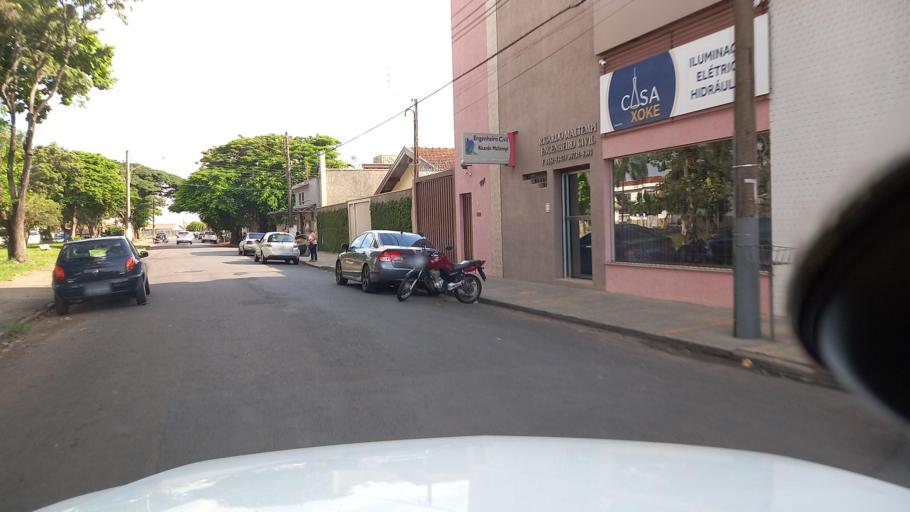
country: BR
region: Sao Paulo
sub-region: Moji-Guacu
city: Mogi-Gaucu
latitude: -22.3488
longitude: -46.9457
